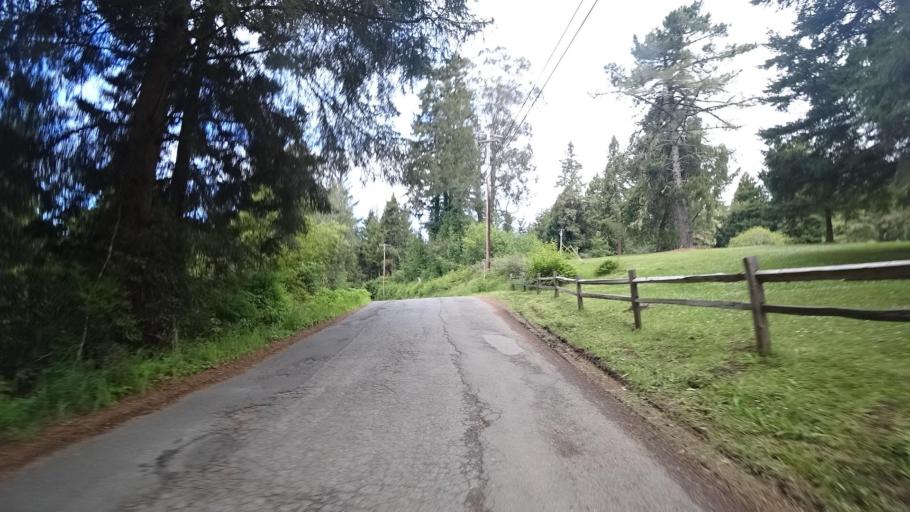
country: US
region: California
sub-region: Humboldt County
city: Bayside
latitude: 40.8482
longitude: -124.0545
